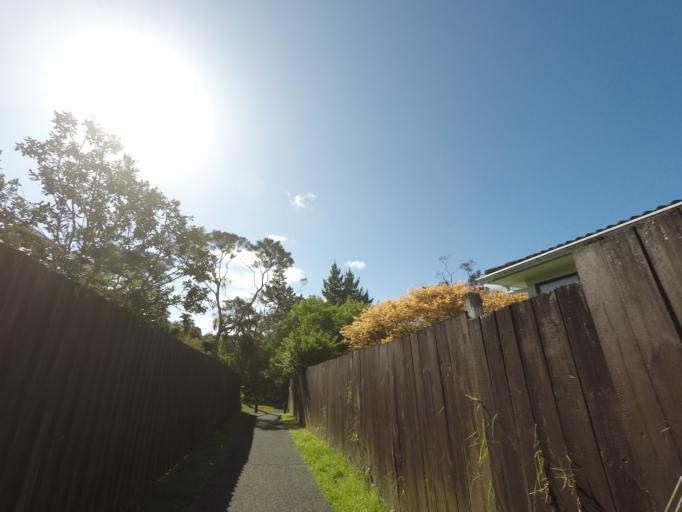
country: NZ
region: Auckland
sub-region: Auckland
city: Rosebank
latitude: -36.8600
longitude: 174.5970
